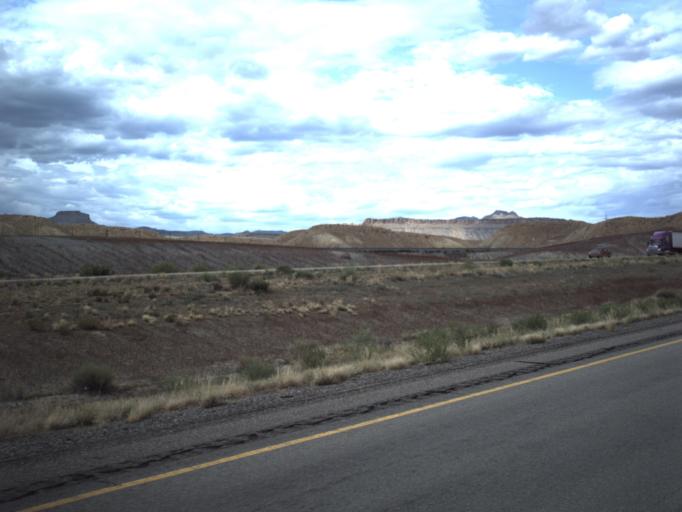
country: US
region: Utah
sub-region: Grand County
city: Moab
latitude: 38.9371
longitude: -109.8369
